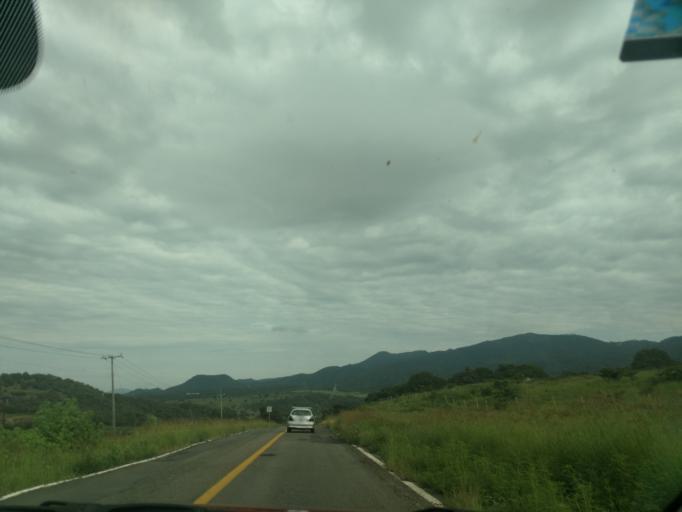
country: MX
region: Jalisco
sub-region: Atengo
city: Soyatlan del Oro
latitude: 20.5464
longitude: -104.2980
